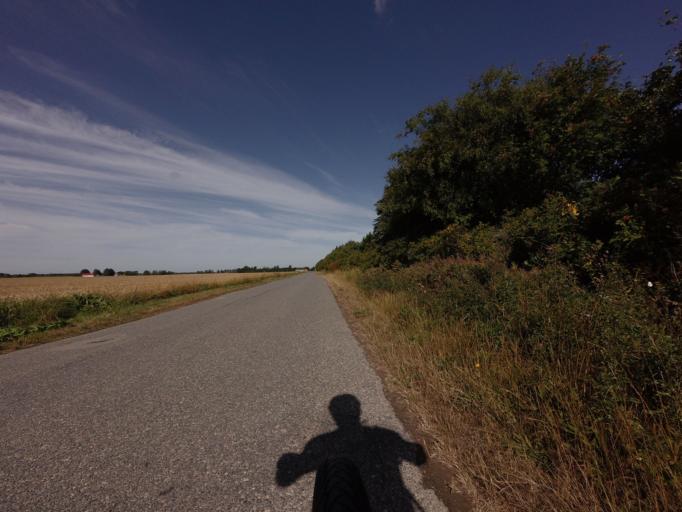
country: DK
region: North Denmark
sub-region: Hjorring Kommune
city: Vra
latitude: 57.3913
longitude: 9.9736
